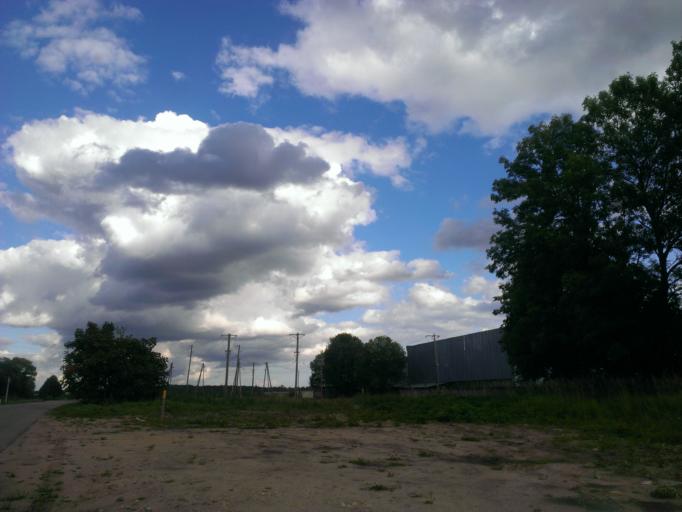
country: LV
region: Sigulda
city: Sigulda
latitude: 57.1562
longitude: 24.8907
